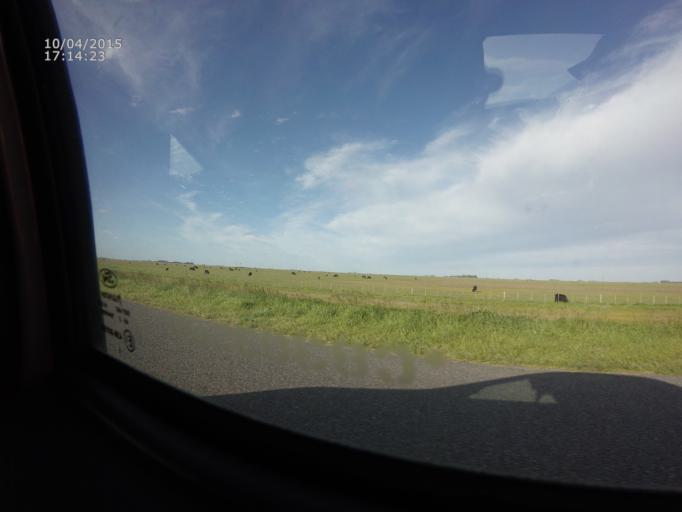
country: AR
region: Buenos Aires
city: Coronel Vidal
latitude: -37.2473
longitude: -57.7860
